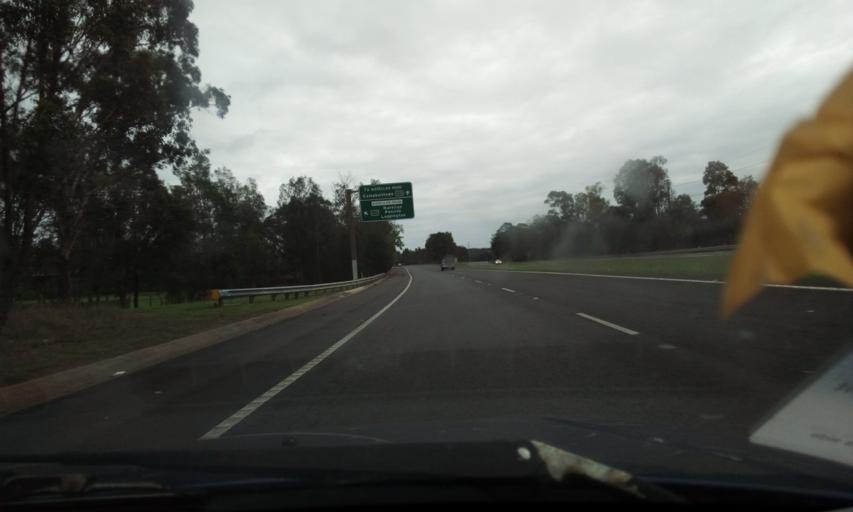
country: AU
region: New South Wales
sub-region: Camden
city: Narellan Vale
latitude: -34.0473
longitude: 150.7433
